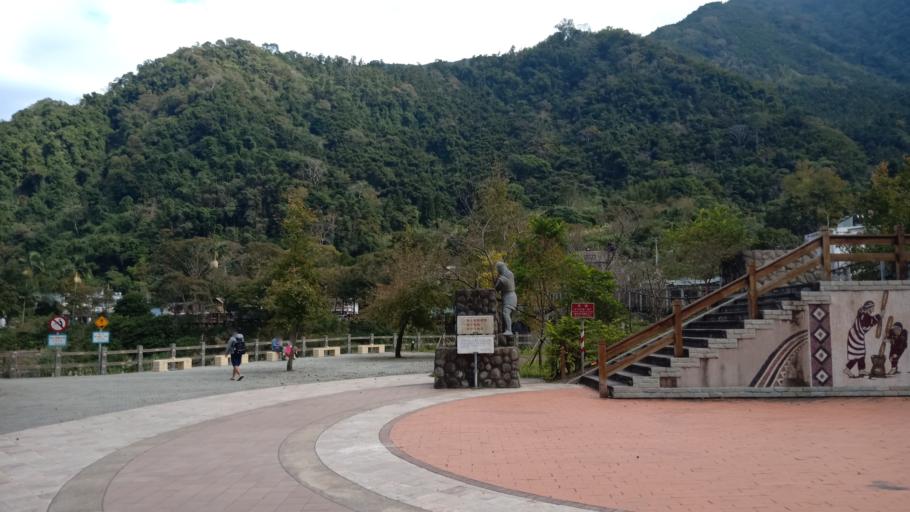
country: TW
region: Taiwan
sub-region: Hsinchu
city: Hsinchu
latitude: 24.5752
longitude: 121.1039
